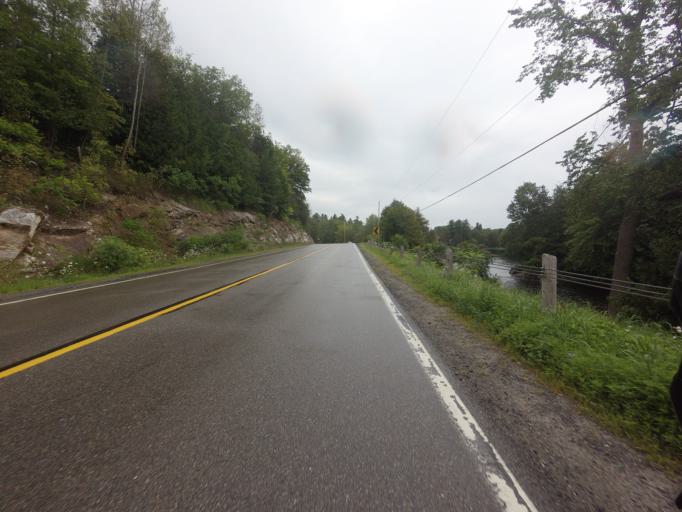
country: CA
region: Ontario
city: Perth
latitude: 44.9715
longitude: -76.4075
